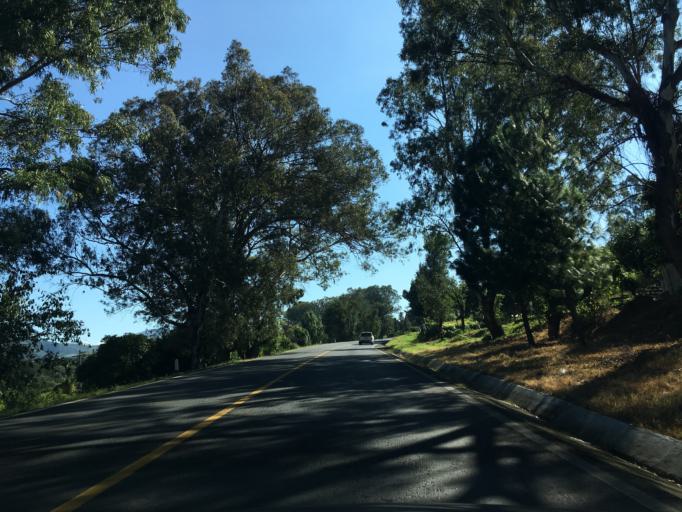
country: MX
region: Michoacan
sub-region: Chilchota
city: Ichan
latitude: 19.8474
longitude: -102.0618
